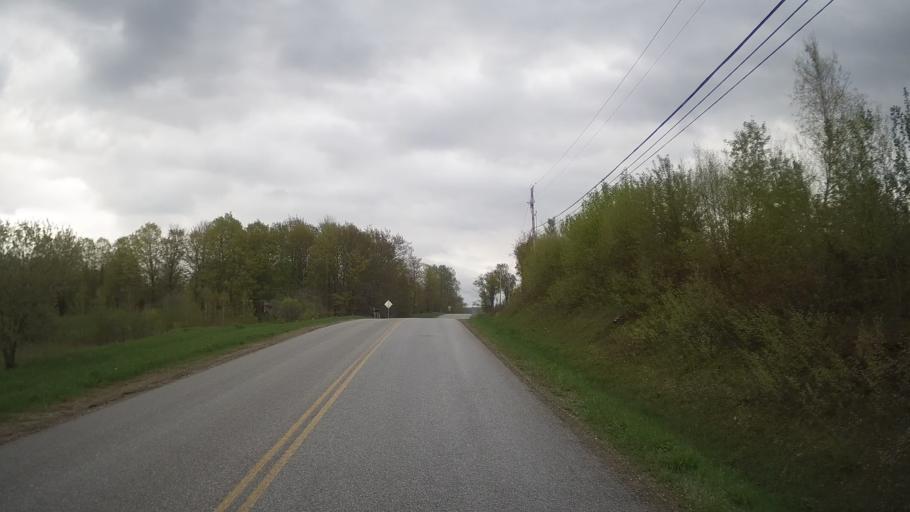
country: US
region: Vermont
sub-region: Franklin County
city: Richford
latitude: 44.9813
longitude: -72.6595
